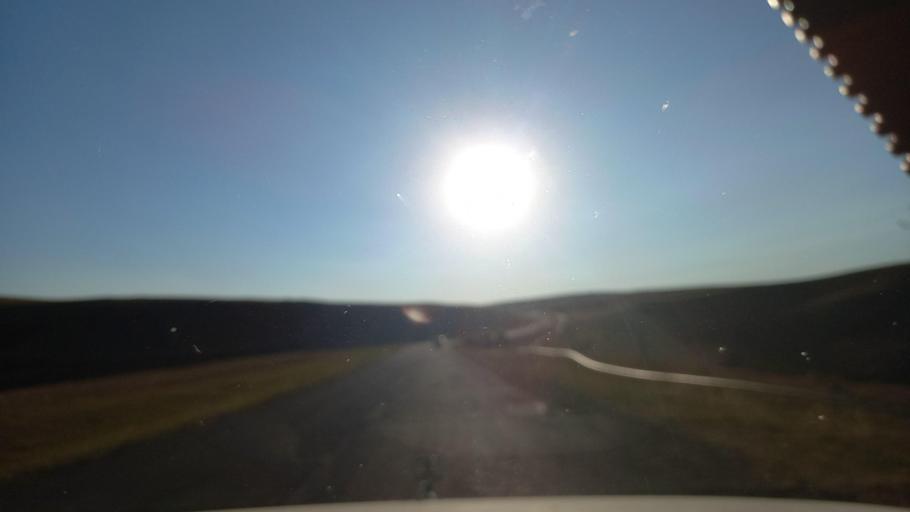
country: AZ
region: Shamkir Rayon
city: Shamkhor
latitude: 40.7638
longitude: 45.9294
